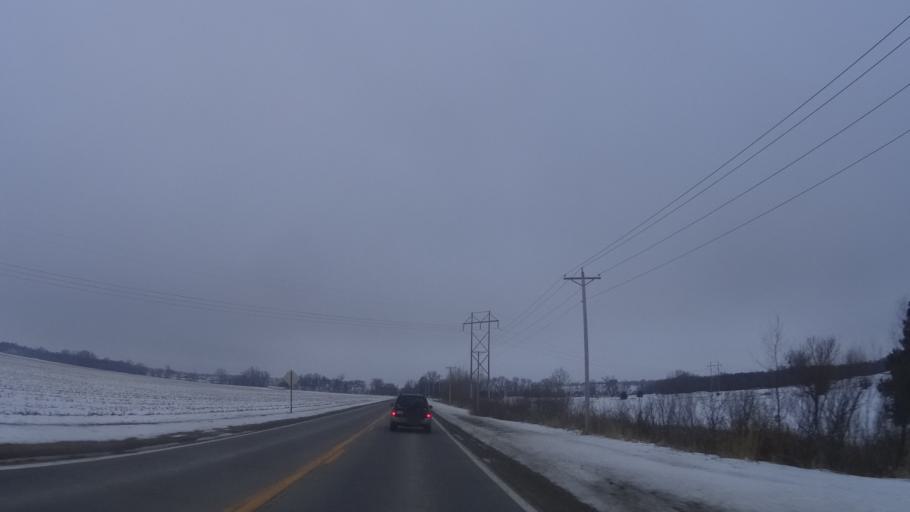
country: US
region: Nebraska
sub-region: Sarpy County
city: La Vista
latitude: 41.1601
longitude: -95.9886
